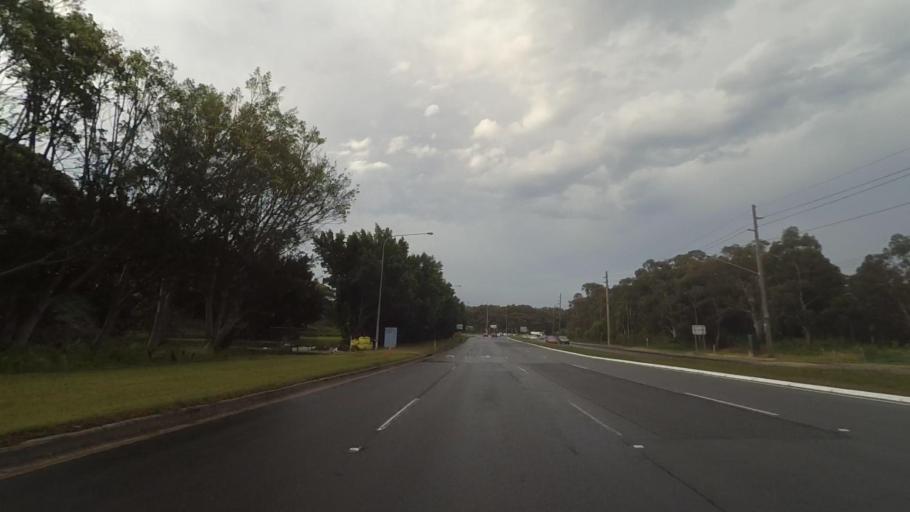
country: AU
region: New South Wales
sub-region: Wollongong
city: Mount Saint Thomas
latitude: -34.4483
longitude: 150.8751
